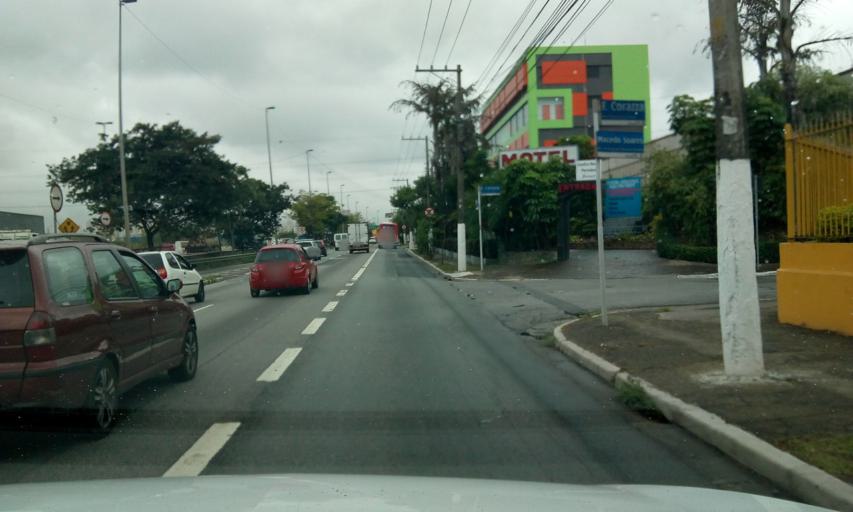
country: BR
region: Sao Paulo
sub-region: Sao Paulo
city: Sao Paulo
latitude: -23.5091
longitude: -46.6995
